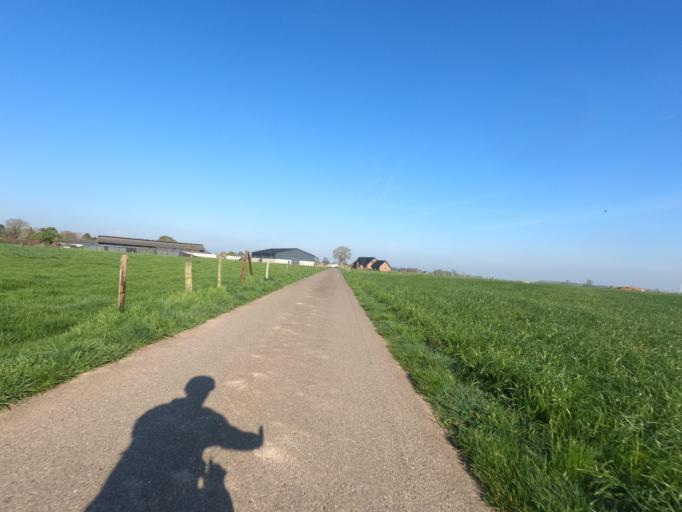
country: DE
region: North Rhine-Westphalia
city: Geilenkirchen
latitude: 51.0092
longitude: 6.1027
